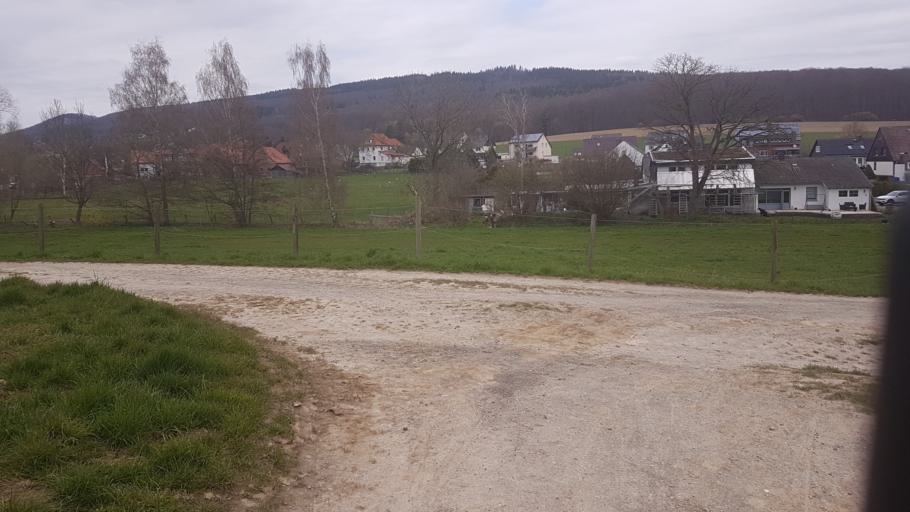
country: DE
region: Lower Saxony
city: Hameln
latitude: 52.1449
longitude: 9.4009
